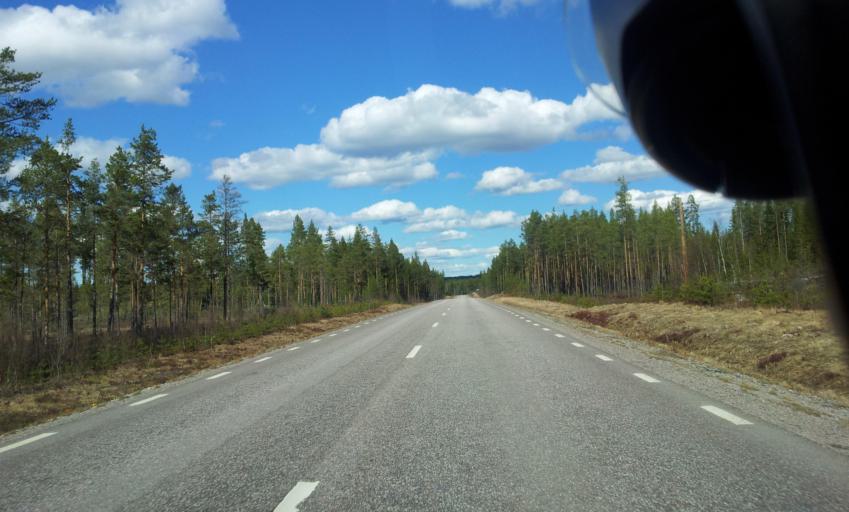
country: SE
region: Gaevleborg
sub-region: Ovanakers Kommun
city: Edsbyn
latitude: 61.2618
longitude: 15.8871
